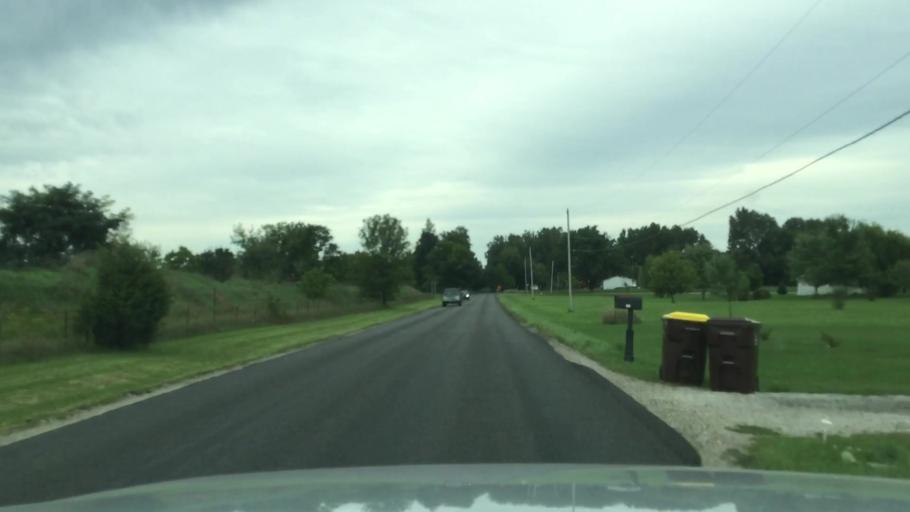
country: US
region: Michigan
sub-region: Shiawassee County
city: Durand
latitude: 42.8751
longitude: -84.0593
